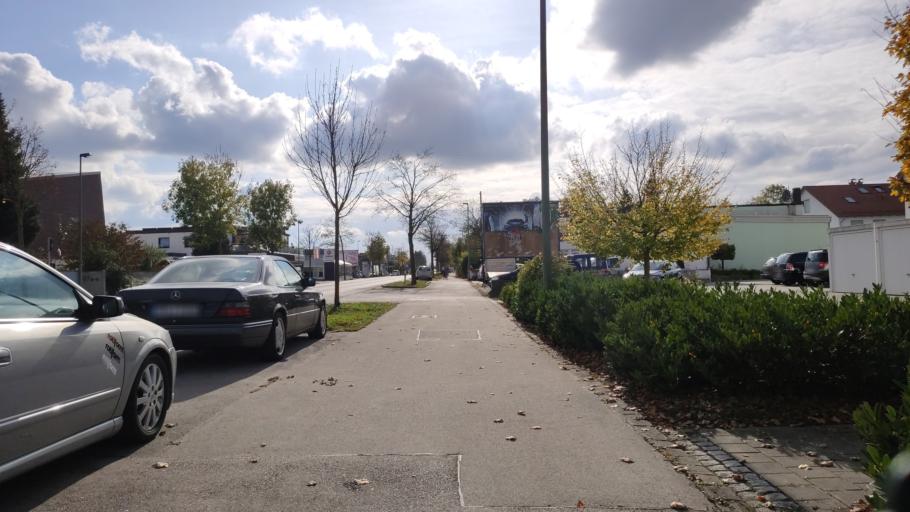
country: DE
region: Bavaria
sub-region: Swabia
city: Konigsbrunn
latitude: 48.2588
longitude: 10.8831
